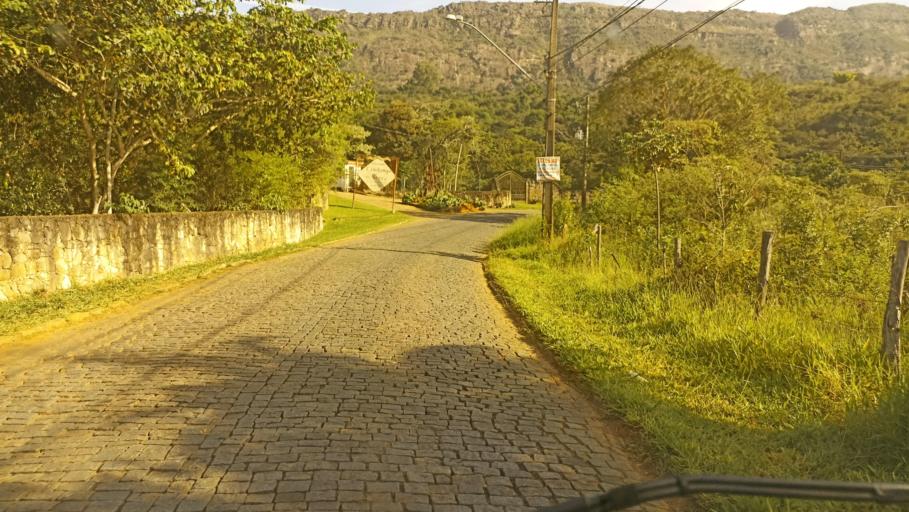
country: BR
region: Minas Gerais
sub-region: Tiradentes
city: Tiradentes
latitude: -21.1145
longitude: -44.1904
